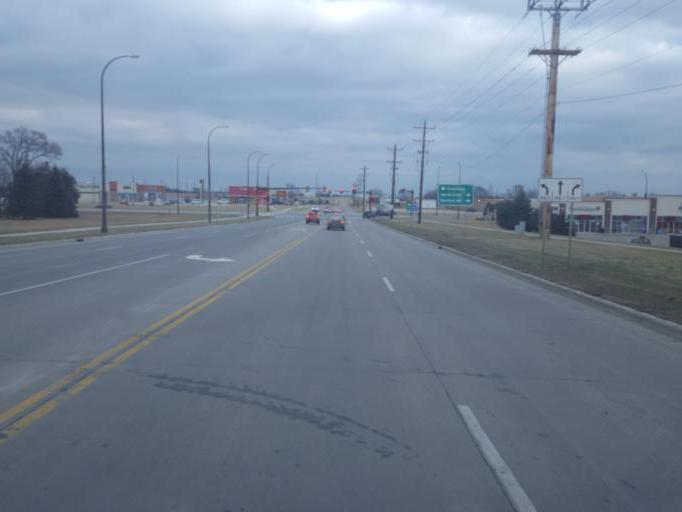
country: US
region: South Dakota
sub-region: Yankton County
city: Yankton
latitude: 42.9088
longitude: -97.3999
